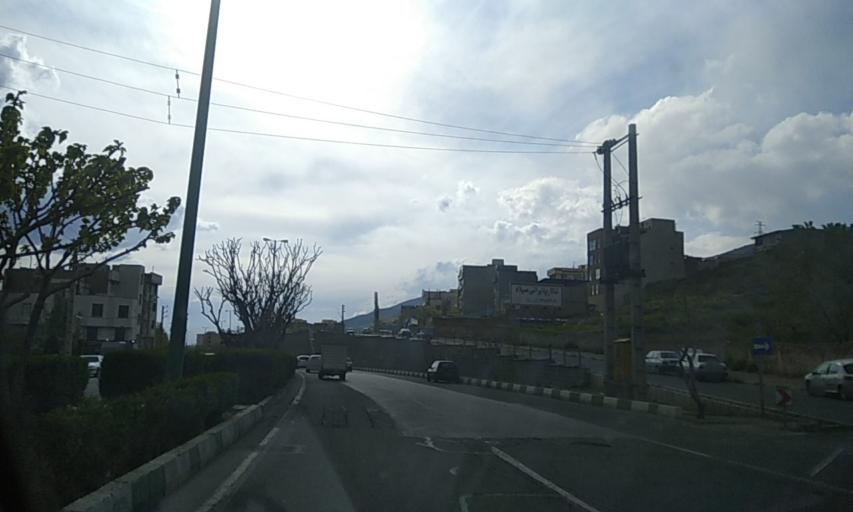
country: IR
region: Tehran
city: Tajrish
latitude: 35.7792
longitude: 51.3097
